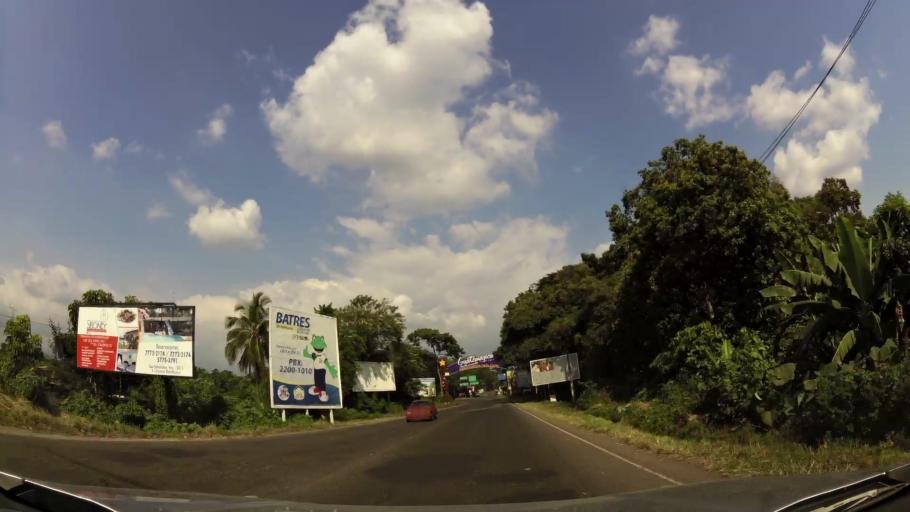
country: GT
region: Retalhuleu
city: San Sebastian
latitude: 14.5721
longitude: -91.6333
